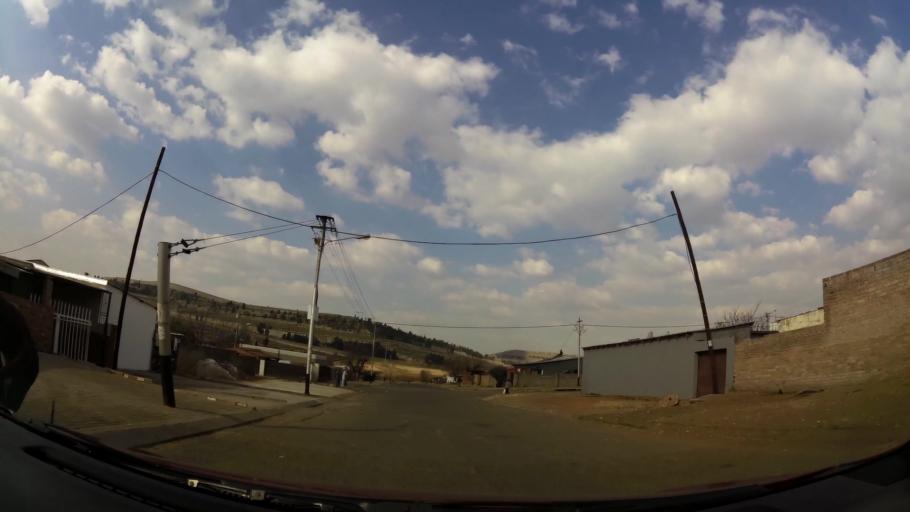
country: ZA
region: Gauteng
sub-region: City of Johannesburg Metropolitan Municipality
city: Soweto
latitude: -26.2287
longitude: 27.9392
